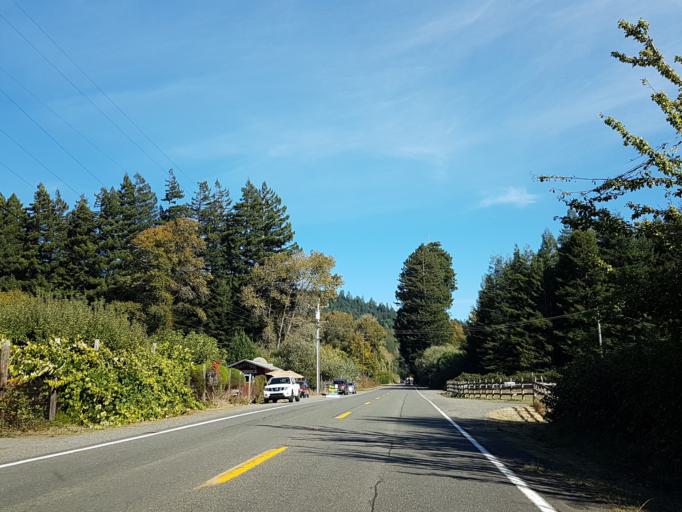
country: US
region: California
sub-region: Humboldt County
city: Rio Dell
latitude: 40.4461
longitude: -123.9968
